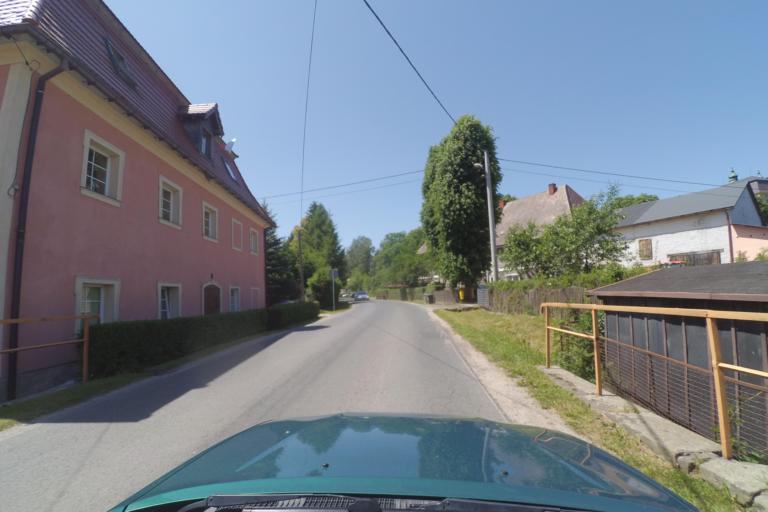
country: PL
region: Lower Silesian Voivodeship
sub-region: Powiat kamiennogorski
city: Krzeszow
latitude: 50.7313
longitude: 16.0714
